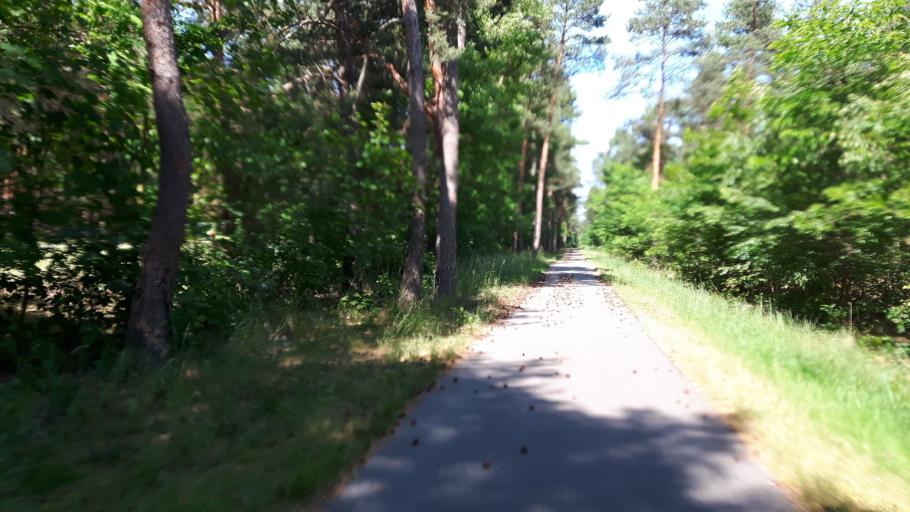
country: DE
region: Brandenburg
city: Treuenbrietzen
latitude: 52.0606
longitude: 12.8254
